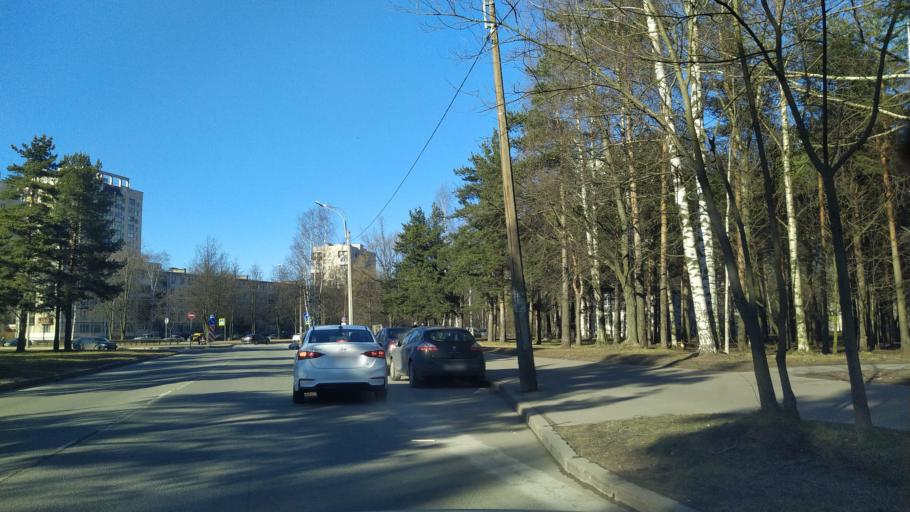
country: RU
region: Leningrad
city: Akademicheskoe
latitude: 60.0039
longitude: 30.4215
